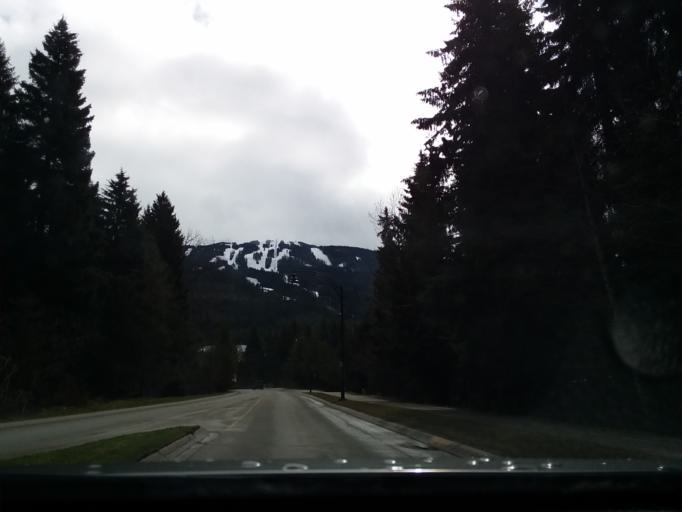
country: CA
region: British Columbia
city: Whistler
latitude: 50.1202
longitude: -122.9508
